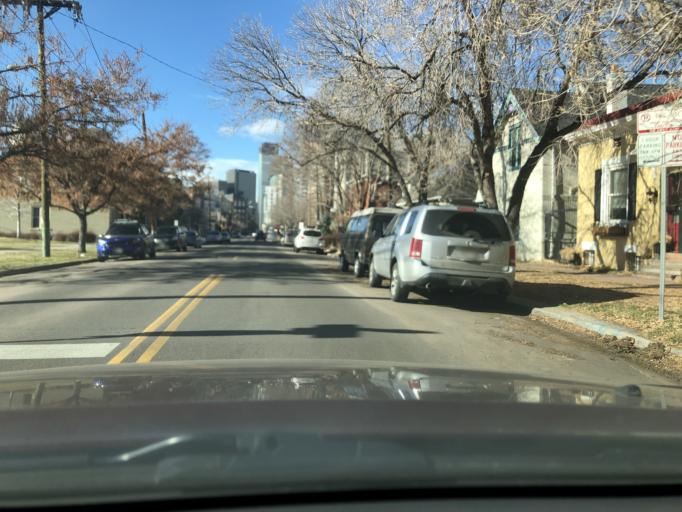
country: US
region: Colorado
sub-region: Denver County
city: Denver
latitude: 39.7474
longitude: -104.9748
